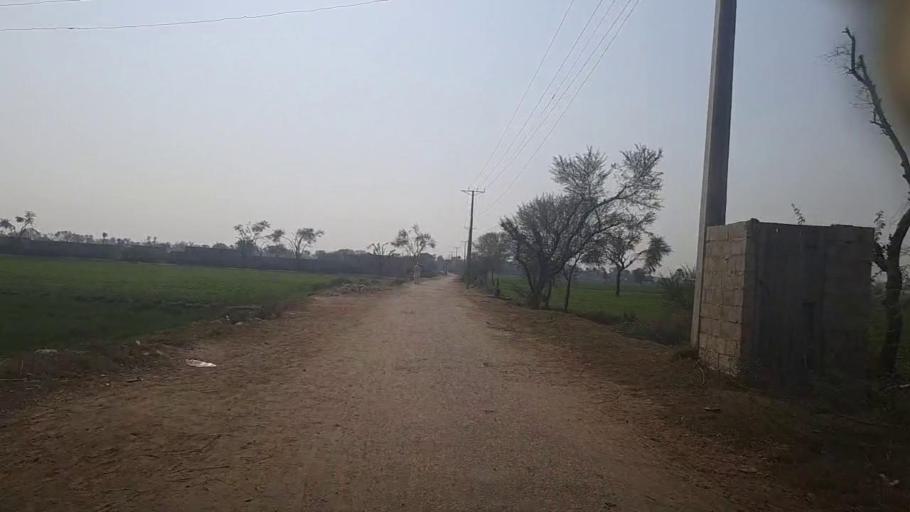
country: PK
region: Sindh
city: Kot Diji
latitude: 27.3549
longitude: 68.7373
